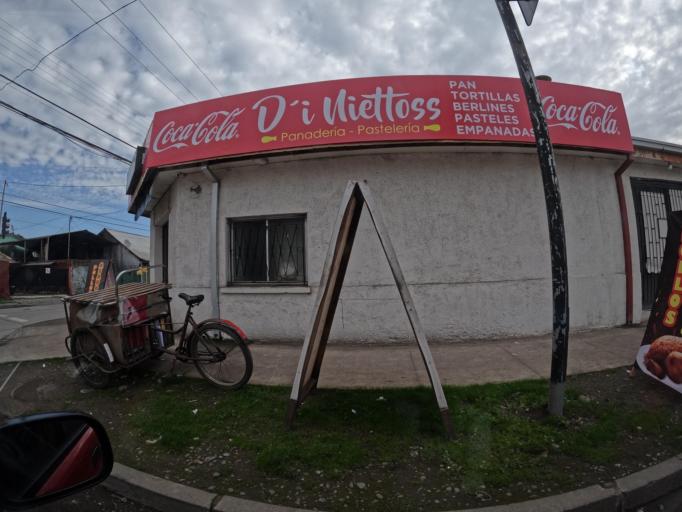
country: CL
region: Maule
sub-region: Provincia de Linares
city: Linares
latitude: -35.8549
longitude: -71.5864
